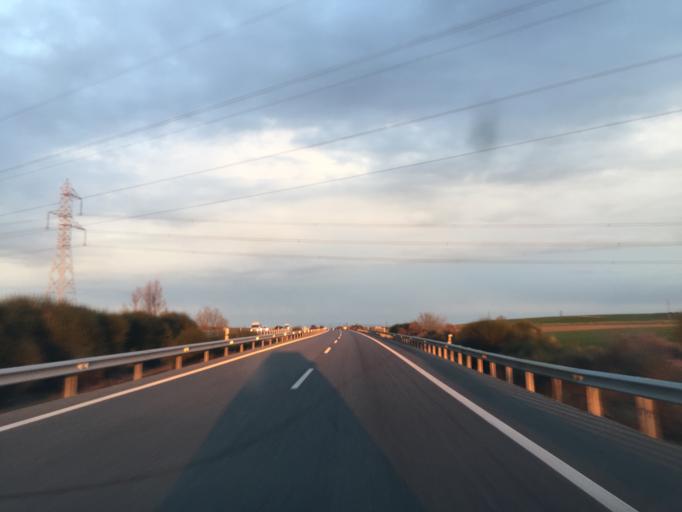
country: ES
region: Castille and Leon
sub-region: Provincia de Burgos
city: Buniel
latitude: 42.3080
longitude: -3.8038
